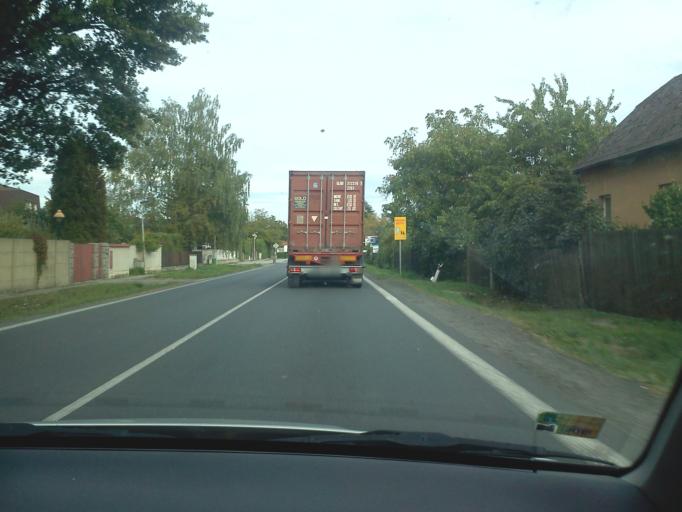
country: CZ
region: Central Bohemia
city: Mukarov
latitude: 49.9898
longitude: 14.7372
